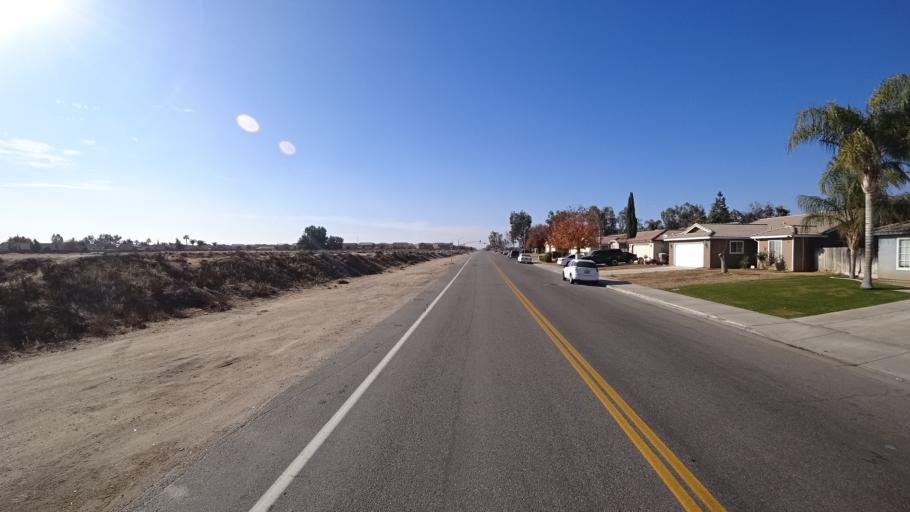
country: US
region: California
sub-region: Kern County
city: Greenfield
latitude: 35.2887
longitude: -119.0533
